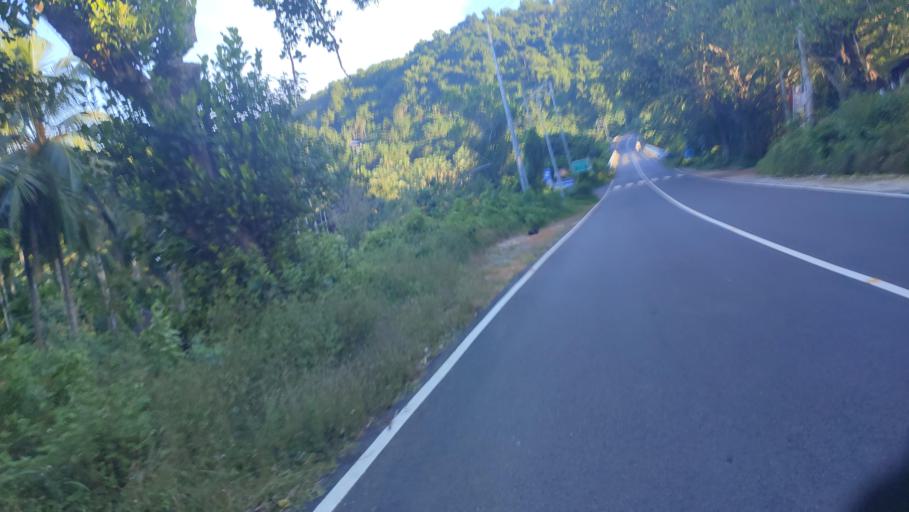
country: IN
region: Kerala
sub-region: Kasaragod District
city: Kasaragod
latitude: 12.4629
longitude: 75.0883
